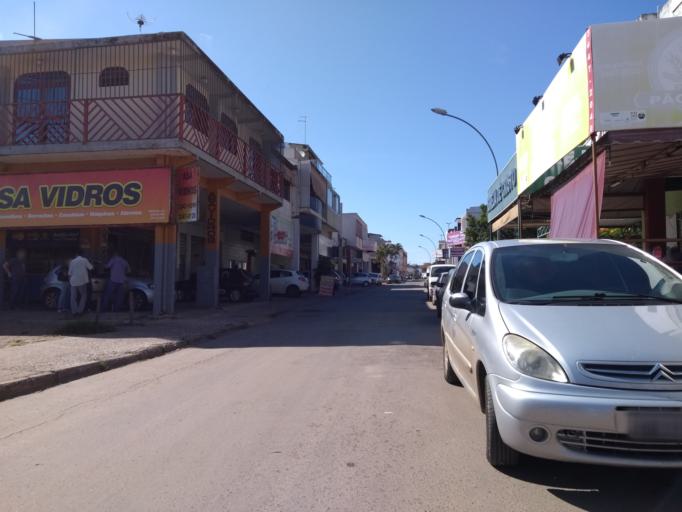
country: BR
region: Federal District
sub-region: Brasilia
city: Brasilia
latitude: -15.7727
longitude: -47.8893
